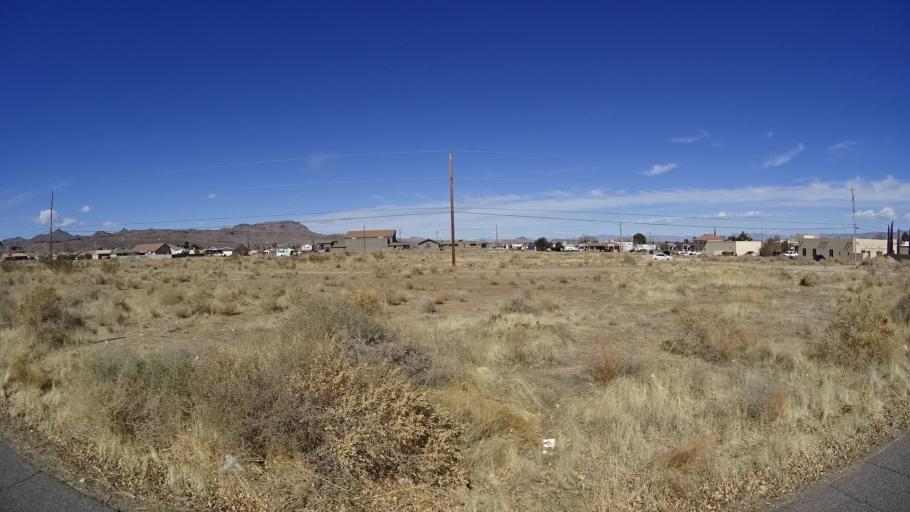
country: US
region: Arizona
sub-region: Mohave County
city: Kingman
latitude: 35.2031
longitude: -114.0355
